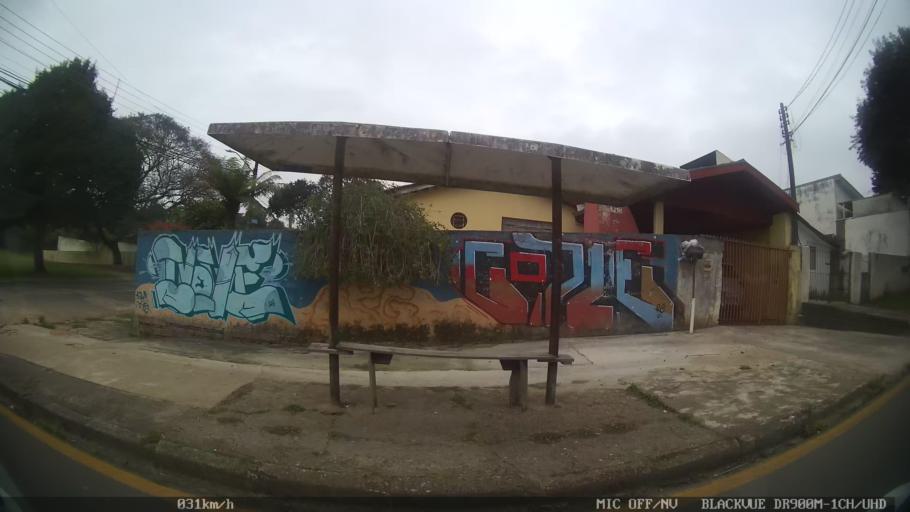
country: BR
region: Parana
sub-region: Almirante Tamandare
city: Almirante Tamandare
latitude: -25.3743
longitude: -49.3282
